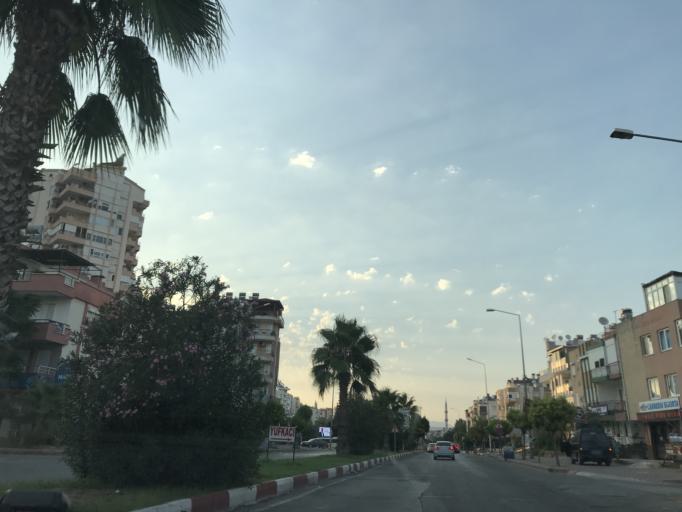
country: TR
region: Antalya
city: Antalya
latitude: 36.8784
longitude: 30.6510
